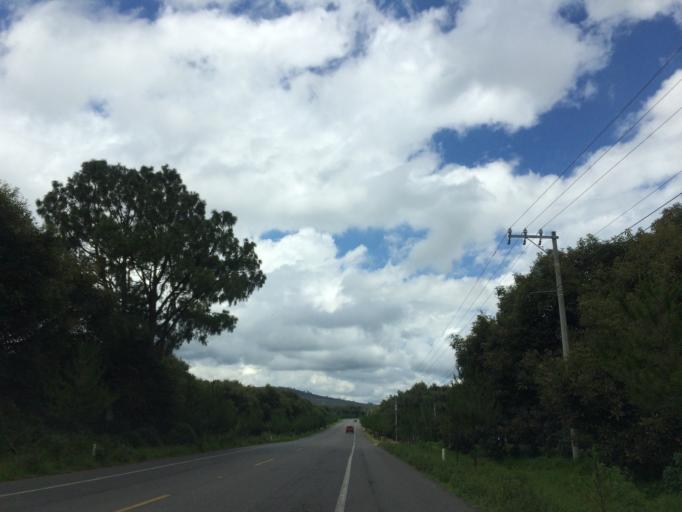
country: MX
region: Michoacan
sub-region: Uruapan
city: Santa Ana Zirosto
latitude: 19.5449
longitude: -102.3201
